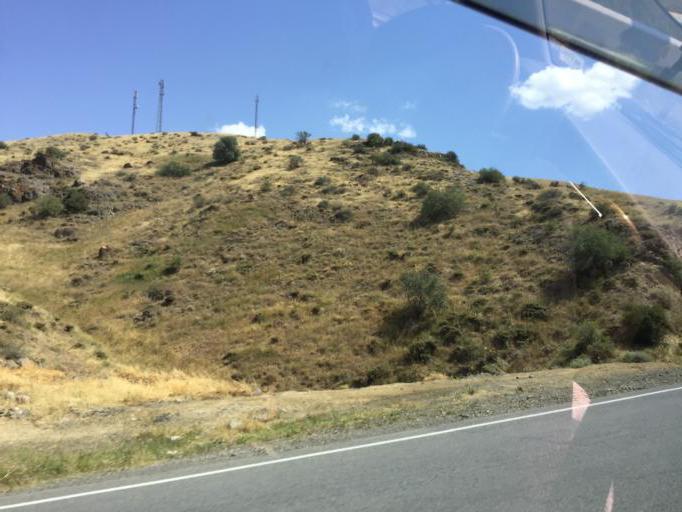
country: AM
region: Vayots' Dzori Marz
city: Jermuk
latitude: 39.7210
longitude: 45.6412
